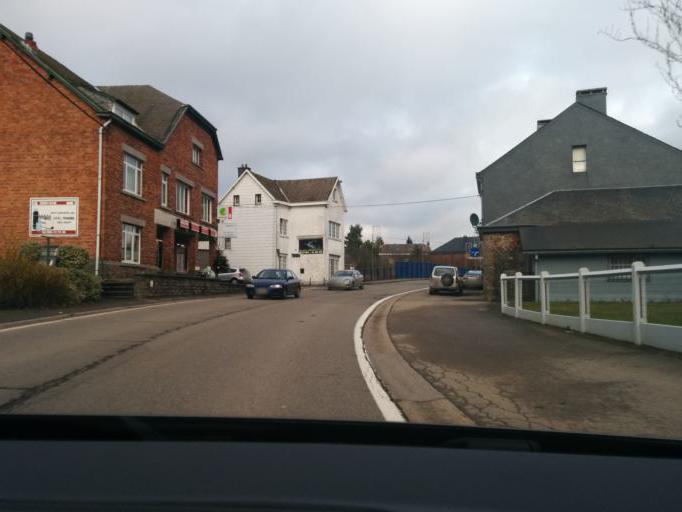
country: BE
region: Wallonia
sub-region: Province du Luxembourg
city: Gouvy
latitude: 50.1908
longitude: 5.9507
